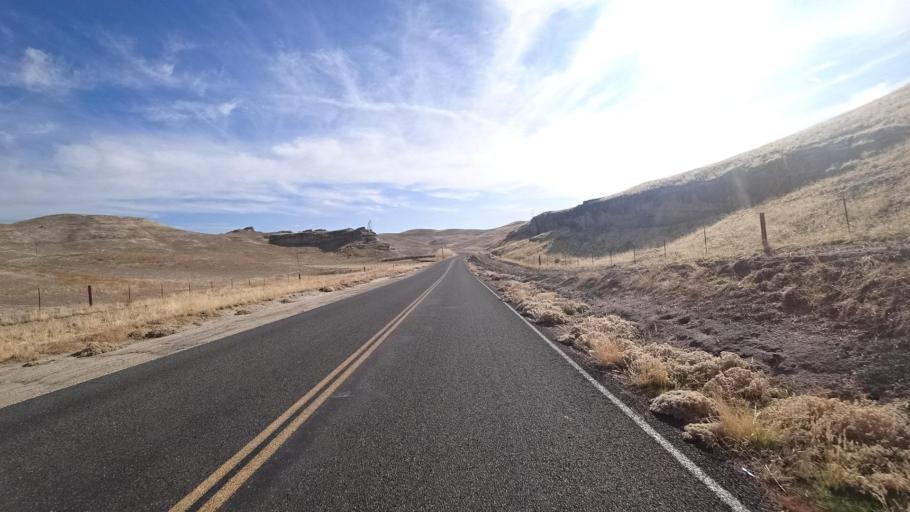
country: US
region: California
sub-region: Kern County
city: Oildale
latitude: 35.6102
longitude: -118.9264
